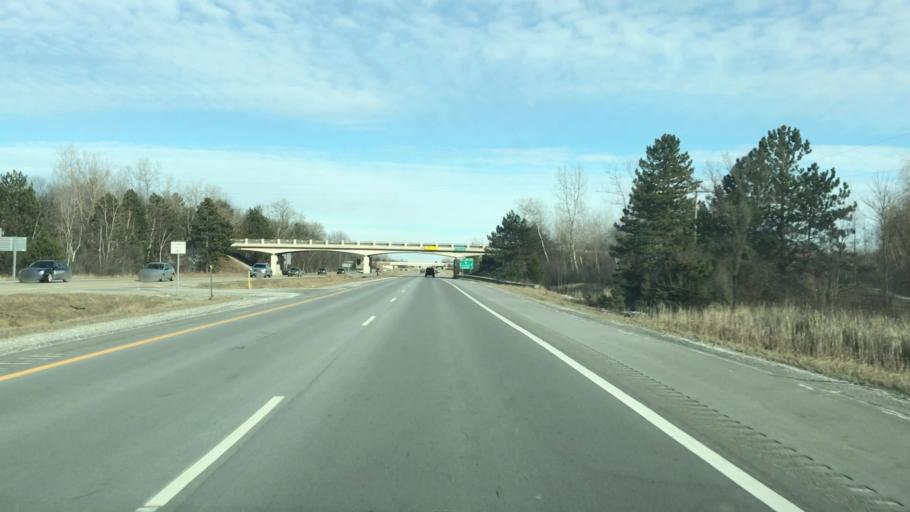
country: US
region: Michigan
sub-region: Saginaw County
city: Freeland
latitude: 43.5978
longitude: -84.1510
